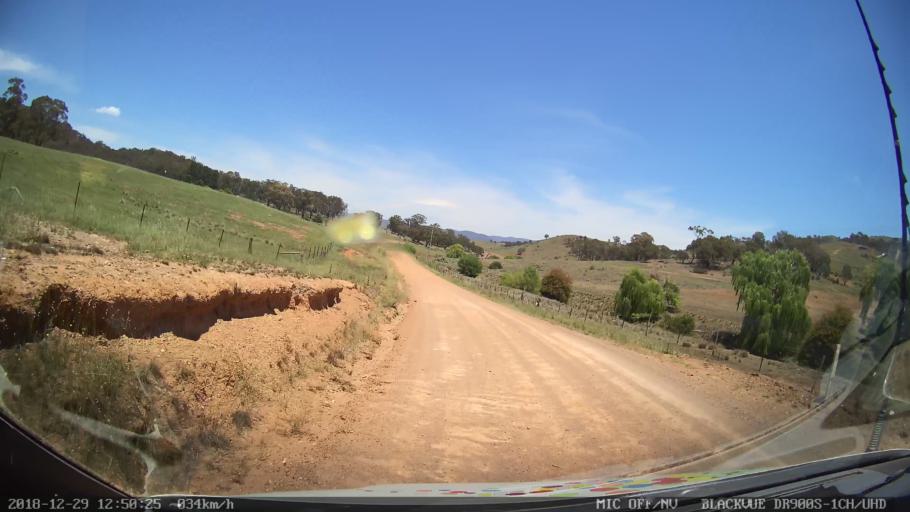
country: AU
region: Australian Capital Territory
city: Macarthur
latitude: -35.6700
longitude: 149.2032
